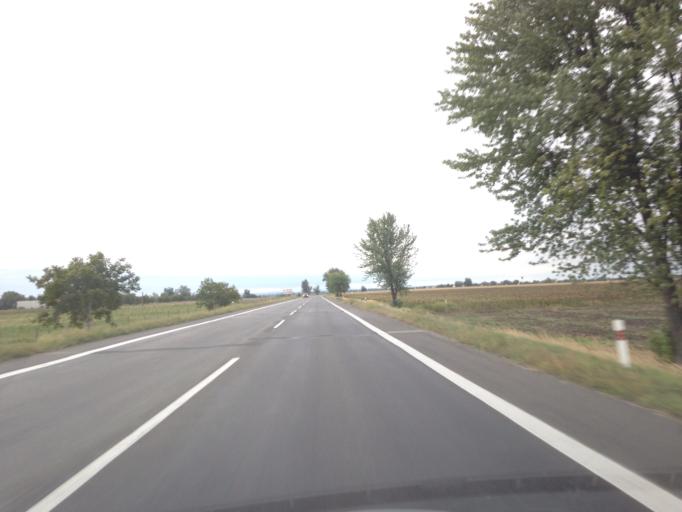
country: SK
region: Nitriansky
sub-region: Okres Komarno
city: Hurbanovo
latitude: 47.8139
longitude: 18.1825
